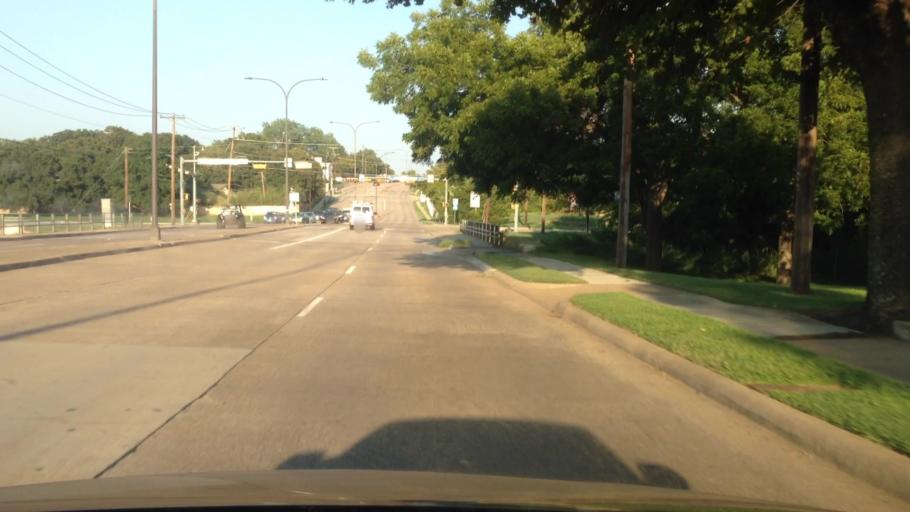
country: US
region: Texas
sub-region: Tarrant County
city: Dalworthington Gardens
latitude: 32.6823
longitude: -97.1786
